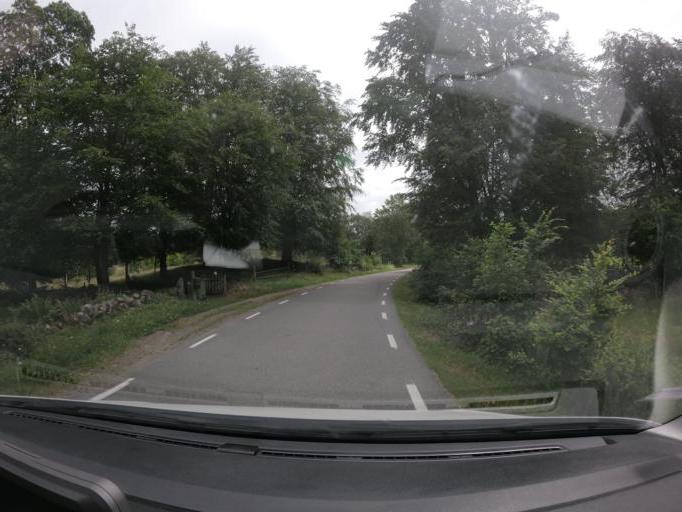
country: SE
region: Skane
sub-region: Hassleholms Kommun
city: Sosdala
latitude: 56.0317
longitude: 13.6223
